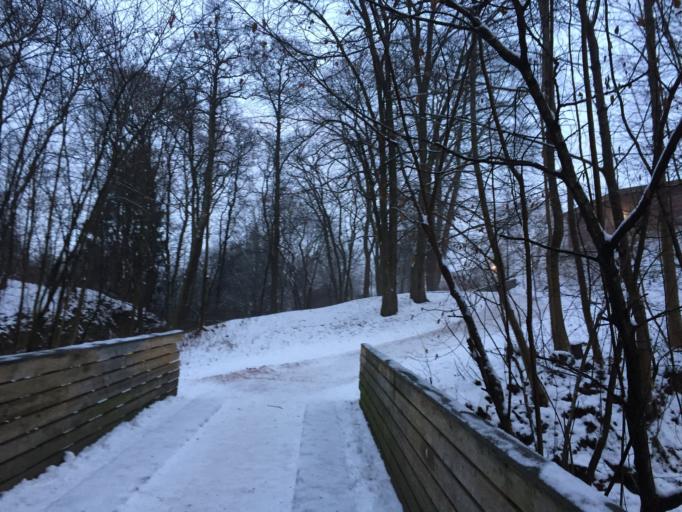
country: NO
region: Oslo
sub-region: Oslo
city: Sjolyststranda
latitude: 59.9234
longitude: 10.6970
